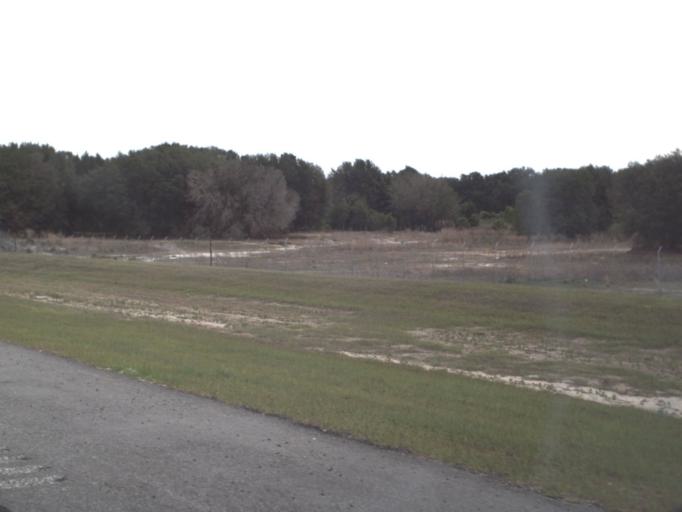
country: US
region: Florida
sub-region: Lake County
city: Mount Plymouth
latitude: 28.7956
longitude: -81.5167
